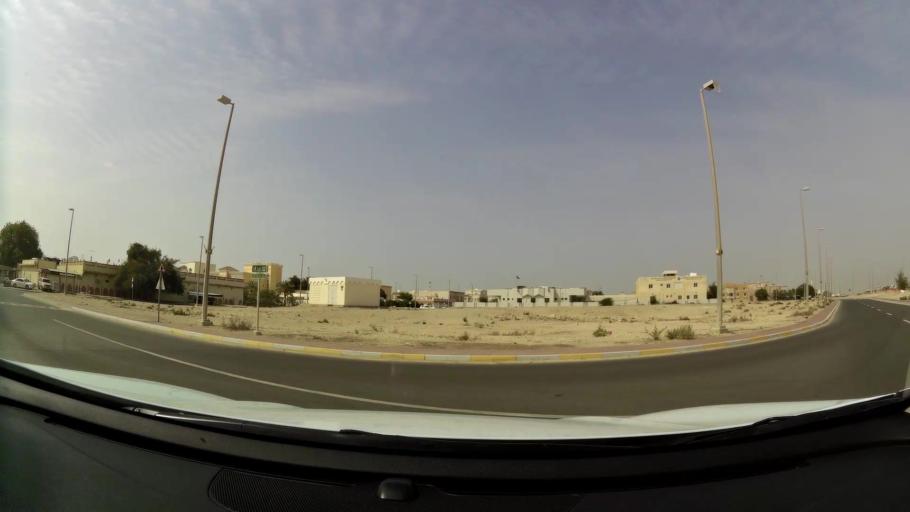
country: AE
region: Abu Dhabi
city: Abu Dhabi
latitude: 24.5468
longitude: 54.6840
